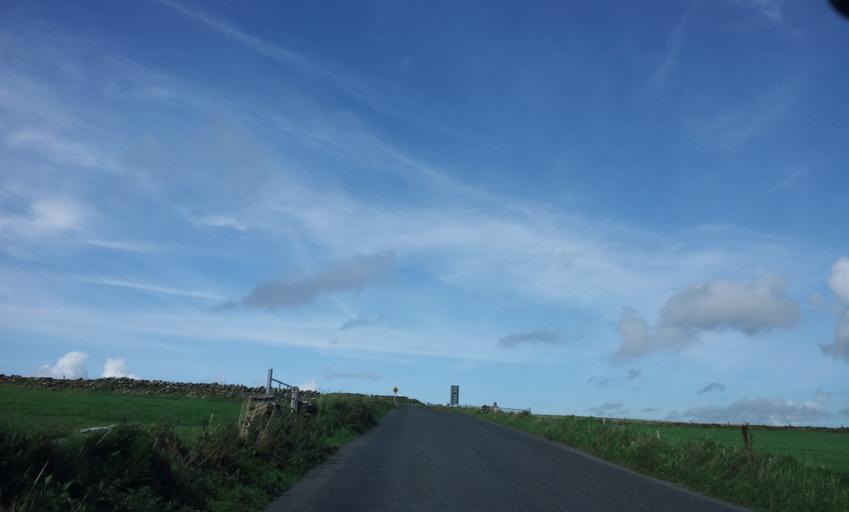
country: IE
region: Munster
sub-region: An Clar
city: Kilrush
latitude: 52.9757
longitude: -9.4220
